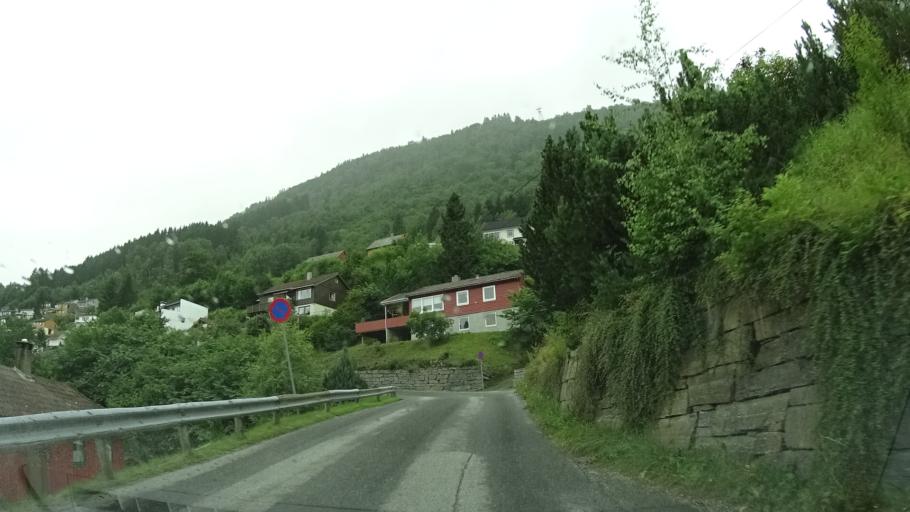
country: NO
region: Hordaland
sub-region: Voss
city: Voss
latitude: 60.6313
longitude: 6.4087
